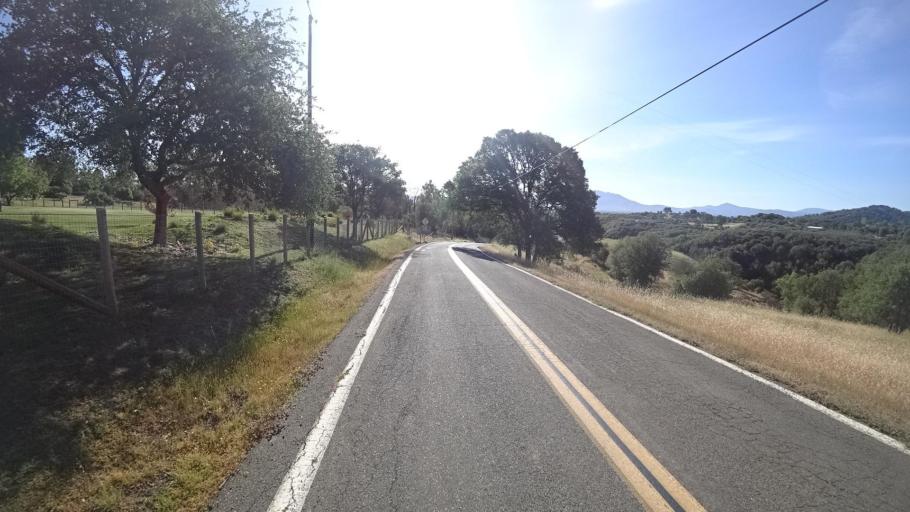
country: US
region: California
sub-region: Lake County
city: Lakeport
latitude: 39.0417
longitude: -122.9503
